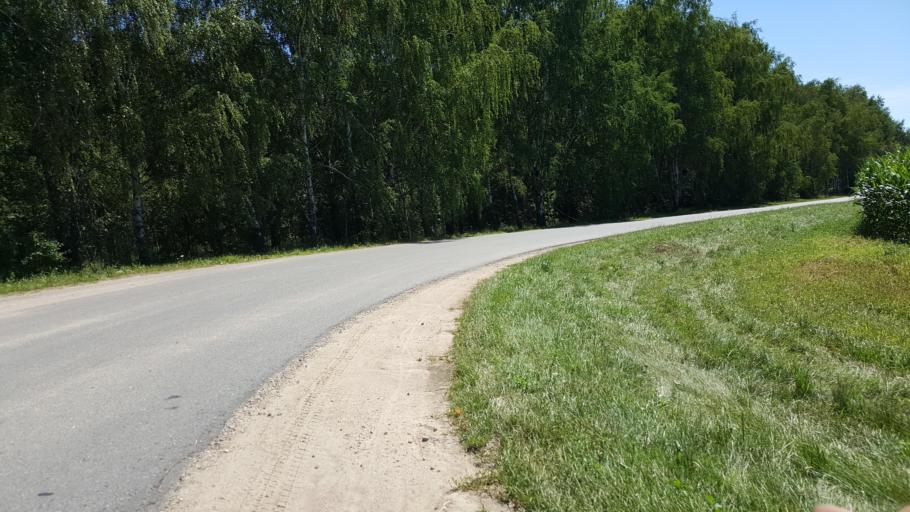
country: BY
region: Brest
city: Charnawchytsy
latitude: 52.2276
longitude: 23.8044
